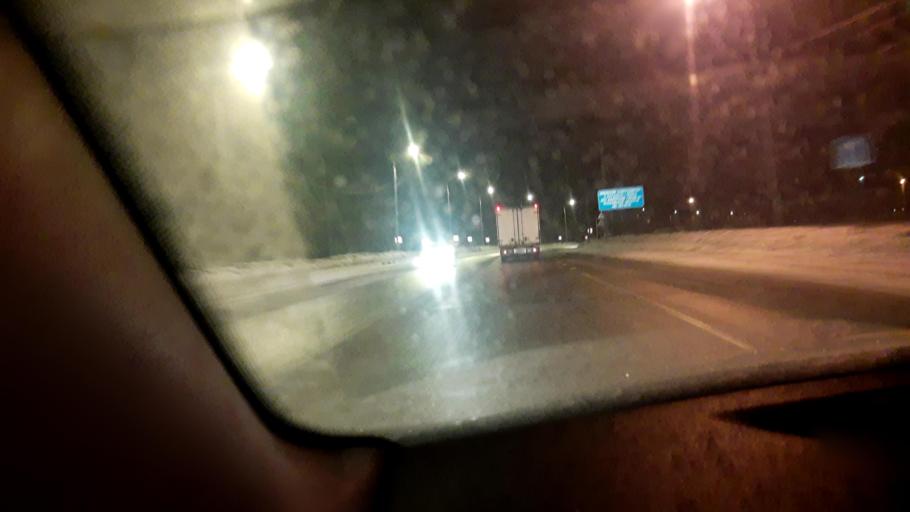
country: RU
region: Moskovskaya
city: Skoropuskovskiy
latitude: 56.3768
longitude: 38.1088
